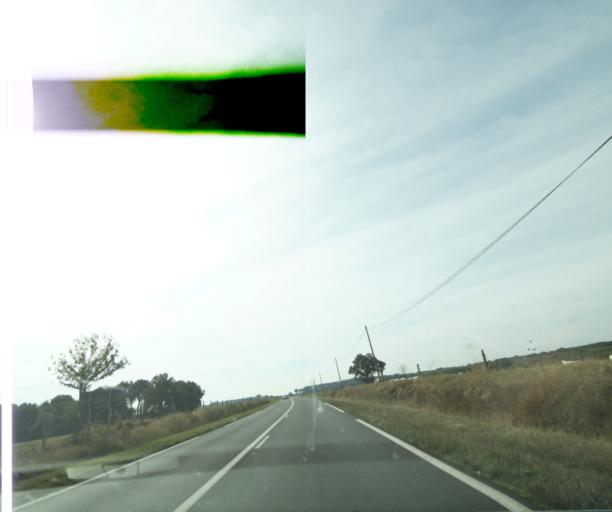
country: FR
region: Auvergne
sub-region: Departement de l'Allier
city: Molinet
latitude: 46.4503
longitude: 3.9154
